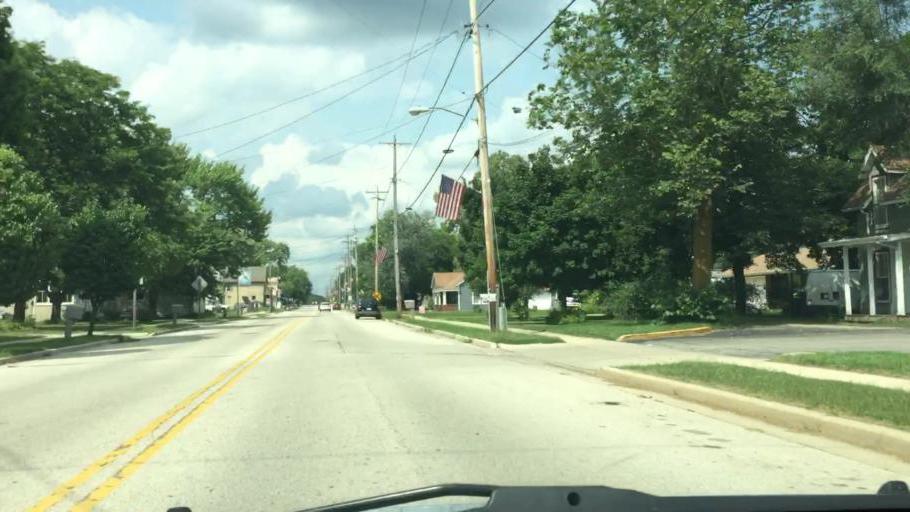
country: US
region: Wisconsin
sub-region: Waukesha County
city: North Prairie
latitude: 42.9328
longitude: -88.4056
